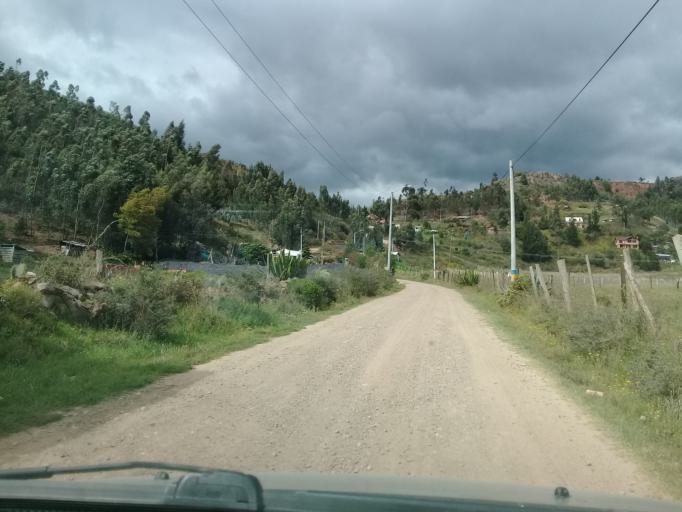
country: CO
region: Cundinamarca
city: Cucunuba
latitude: 5.2552
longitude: -73.7662
